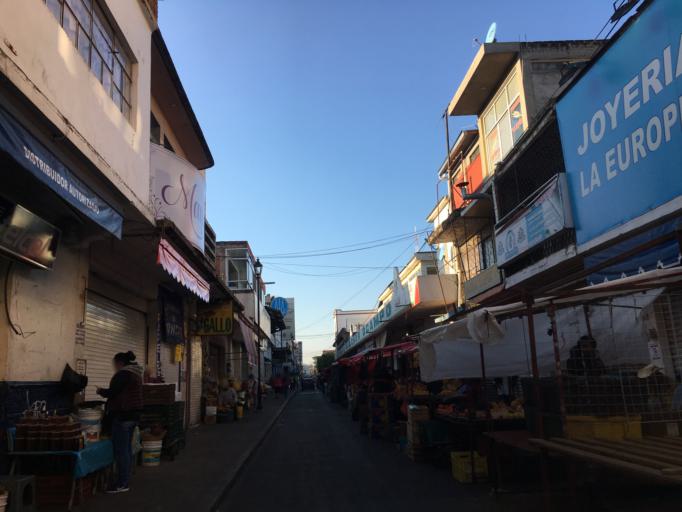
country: MX
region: Michoacan
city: Heroica Zitacuaro
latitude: 19.4378
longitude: -100.3567
